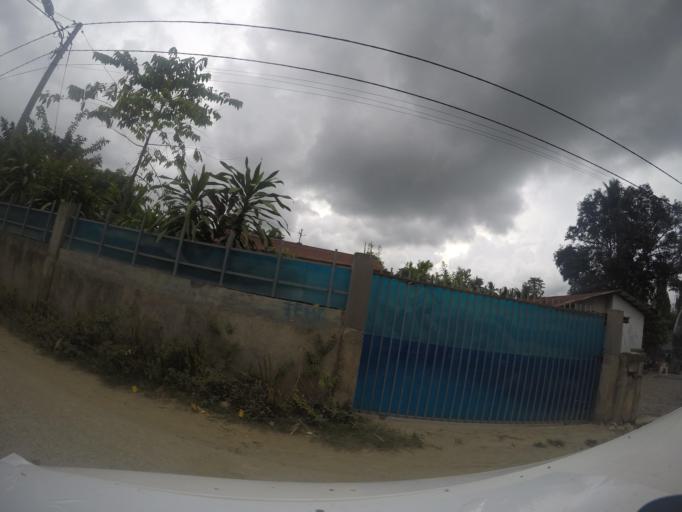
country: TL
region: Viqueque
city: Viqueque
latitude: -8.8604
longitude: 126.3634
